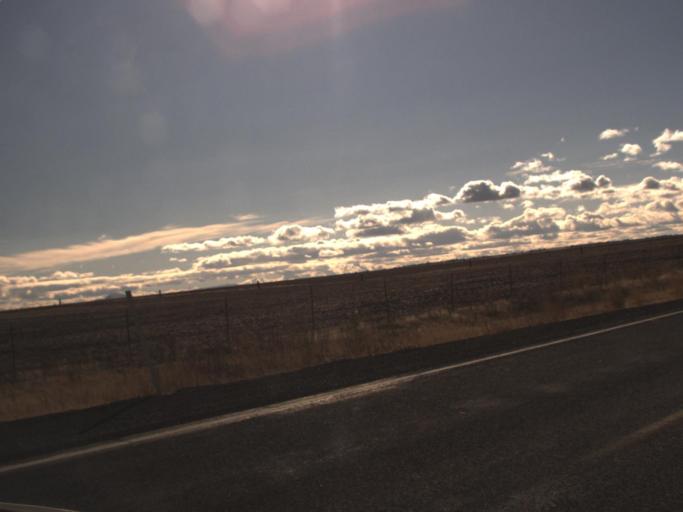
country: US
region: Washington
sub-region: Asotin County
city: Asotin
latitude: 46.1746
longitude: -117.0816
